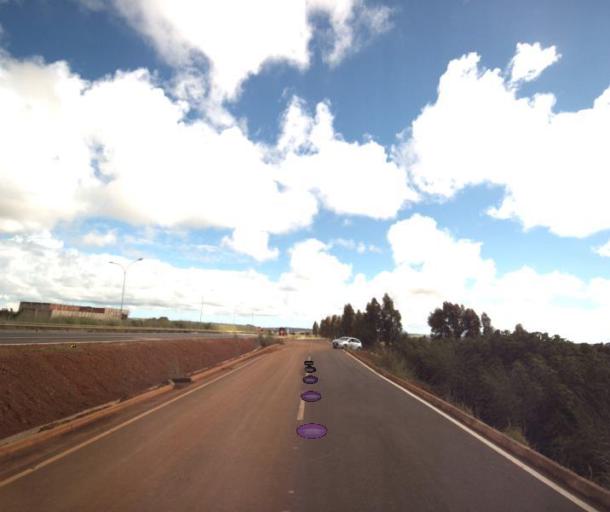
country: BR
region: Goias
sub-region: Anapolis
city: Anapolis
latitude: -16.2316
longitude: -49.0080
